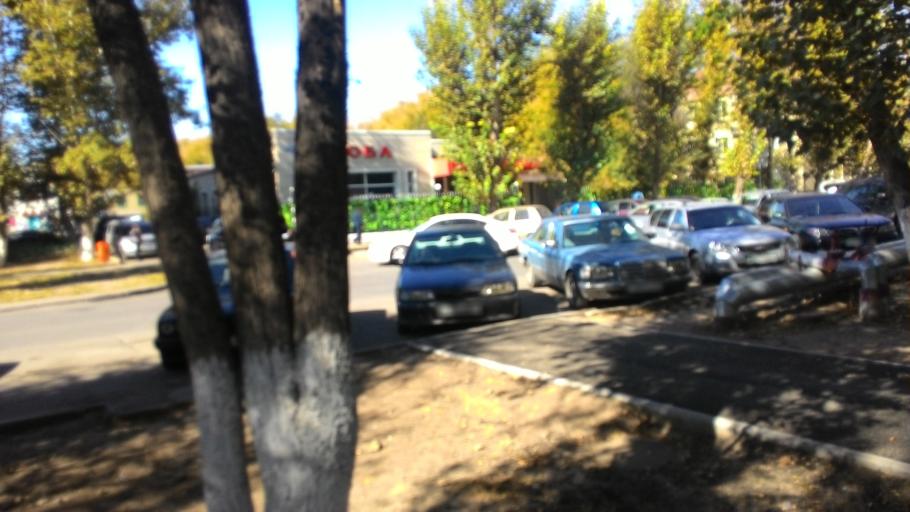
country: KZ
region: Astana Qalasy
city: Astana
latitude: 51.1771
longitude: 71.4135
